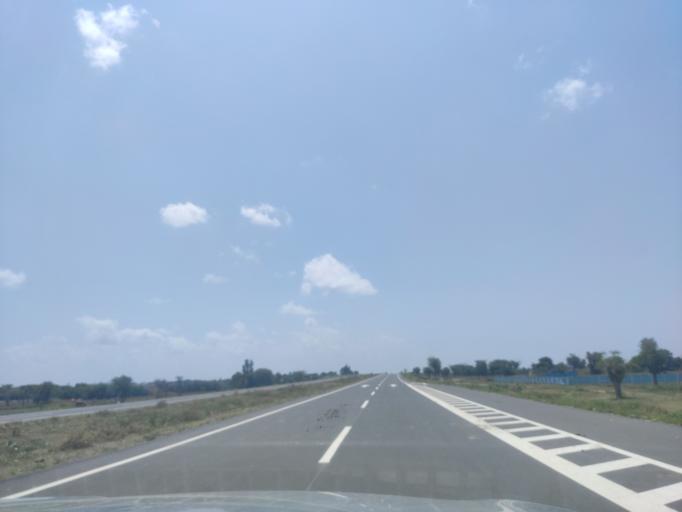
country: ET
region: Oromiya
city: Mojo
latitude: 8.3421
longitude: 38.9737
